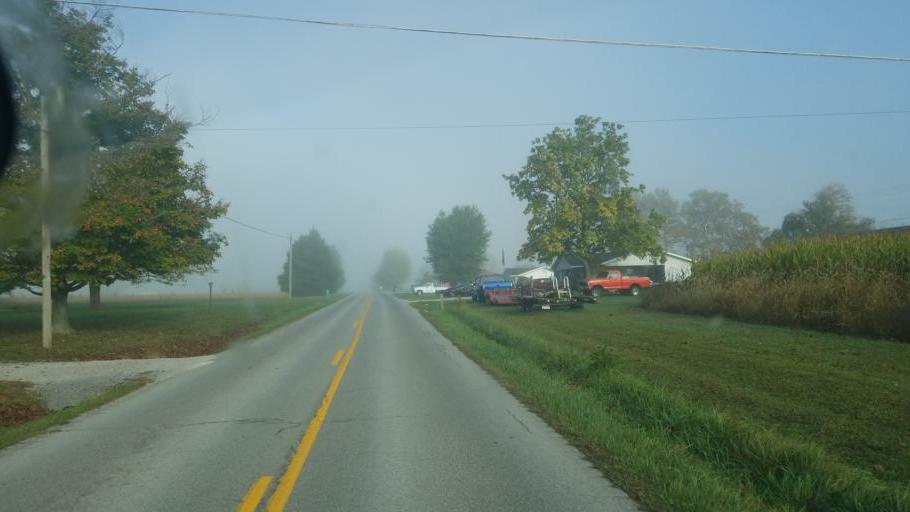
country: US
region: Kentucky
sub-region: Fleming County
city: Flemingsburg
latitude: 38.4832
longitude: -83.6097
